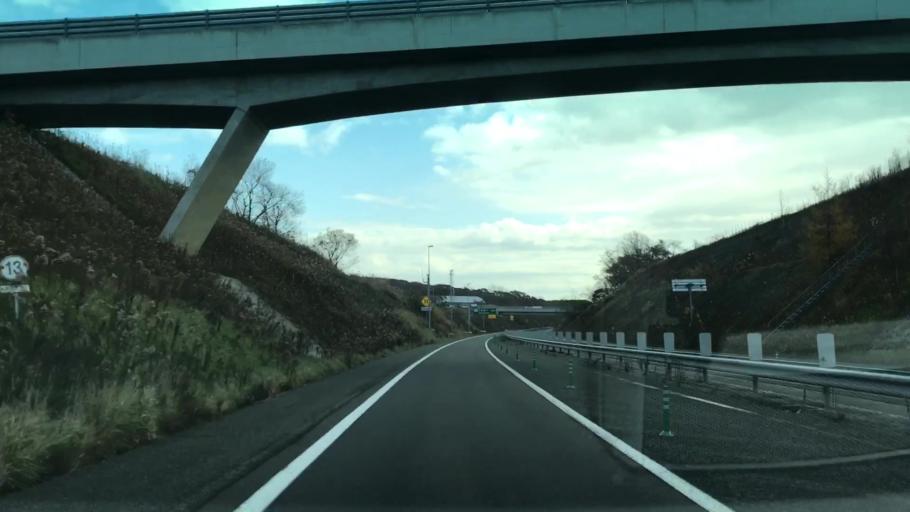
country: JP
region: Hokkaido
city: Shizunai-furukawacho
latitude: 42.5419
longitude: 142.0130
